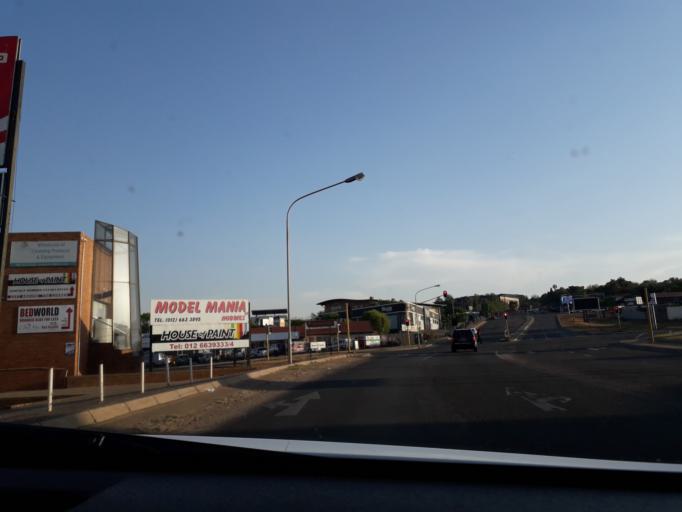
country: ZA
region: Gauteng
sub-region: City of Tshwane Metropolitan Municipality
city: Centurion
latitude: -25.8622
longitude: 28.1906
